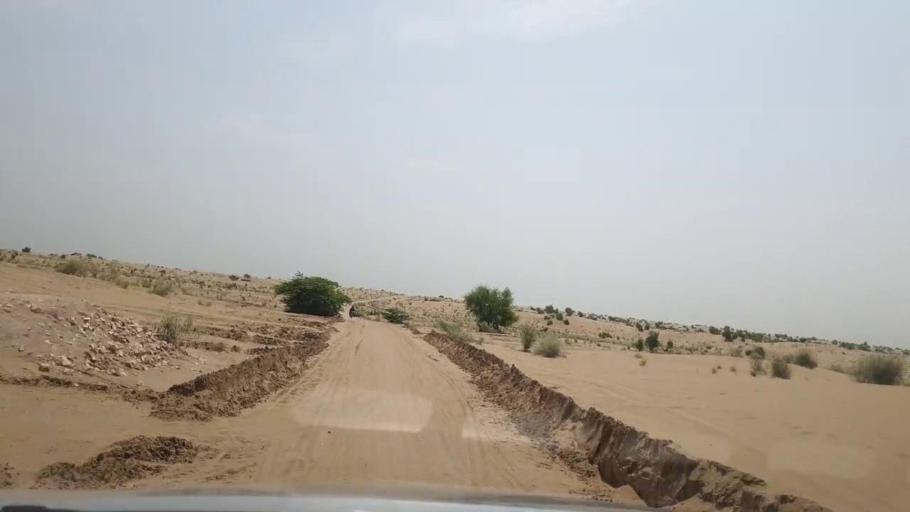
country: PK
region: Sindh
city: Pano Aqil
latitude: 27.5827
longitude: 69.1635
